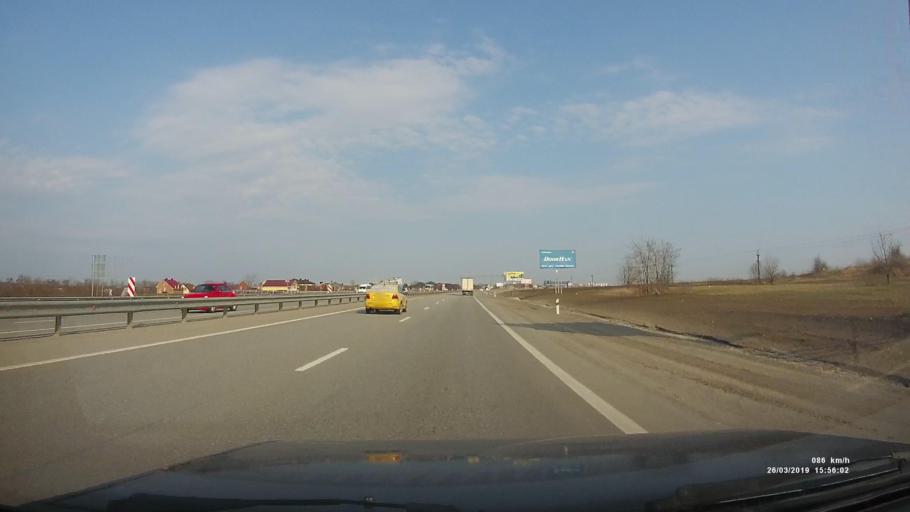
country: RU
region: Rostov
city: Kalinin
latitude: 47.2666
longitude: 39.5805
